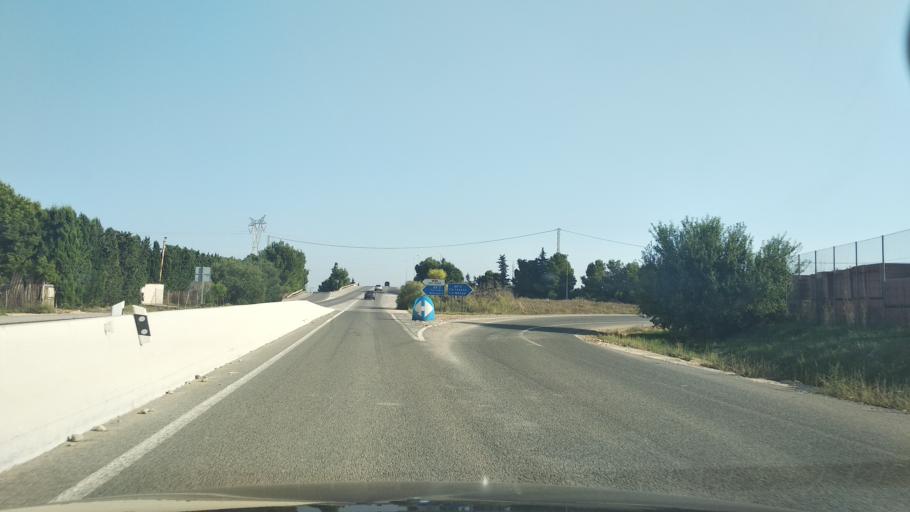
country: ES
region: Murcia
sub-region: Murcia
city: San Javier
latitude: 37.8176
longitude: -0.8452
